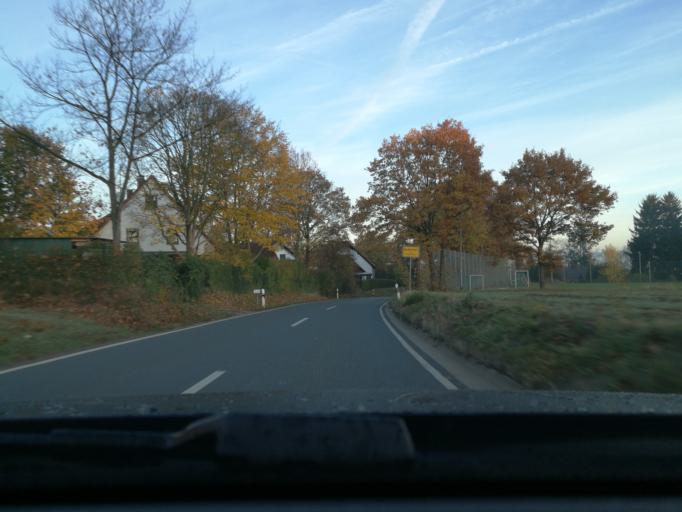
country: DE
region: Bavaria
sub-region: Regierungsbezirk Mittelfranken
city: Obermichelbach
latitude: 49.5556
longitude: 10.9210
